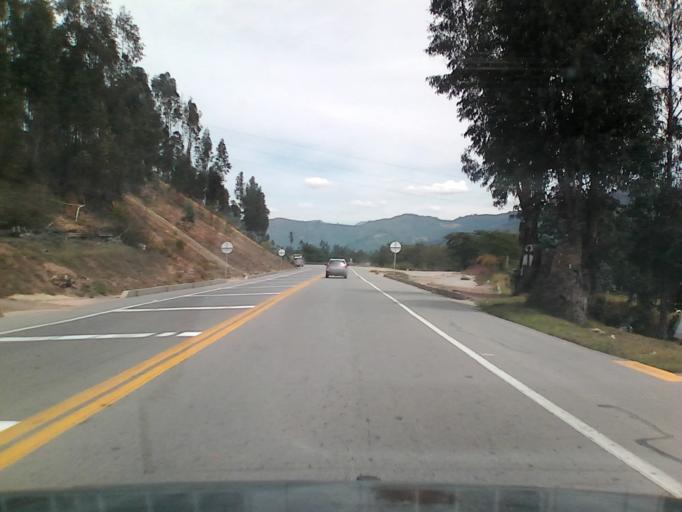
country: CO
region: Boyaca
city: Tibasosa
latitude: 5.7653
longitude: -72.9967
